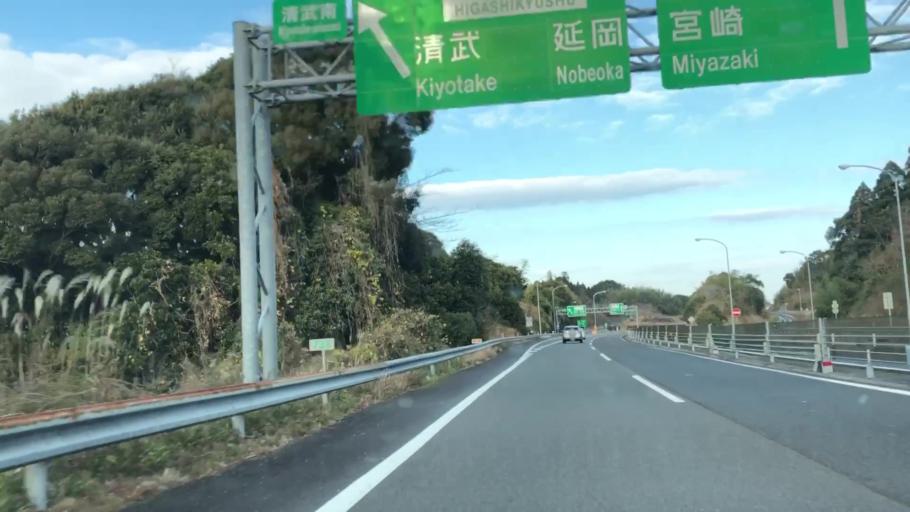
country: JP
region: Miyazaki
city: Miyazaki-shi
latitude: 31.8451
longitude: 131.3527
